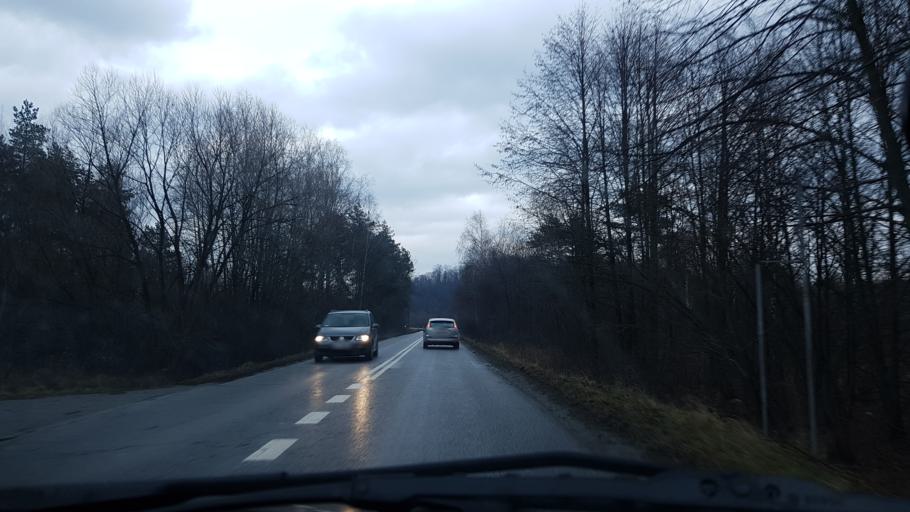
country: PL
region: Silesian Voivodeship
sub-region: Powiat zywiecki
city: Lekawica
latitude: 49.7115
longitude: 19.2558
